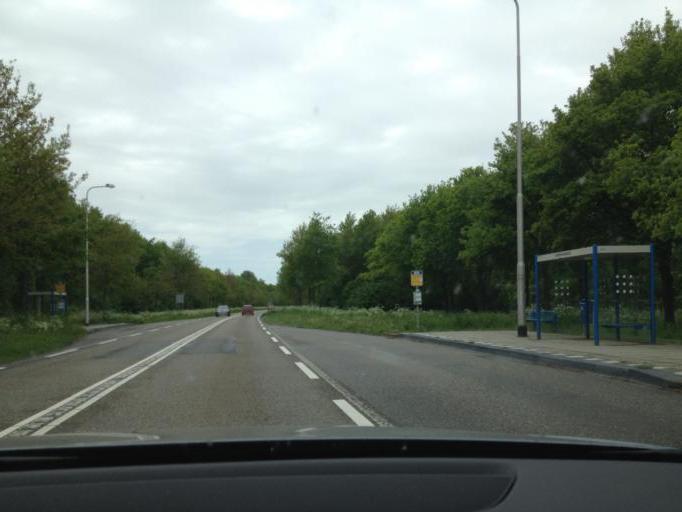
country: NL
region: North Holland
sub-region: Gemeente Huizen
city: Huizen
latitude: 52.3416
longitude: 5.2649
